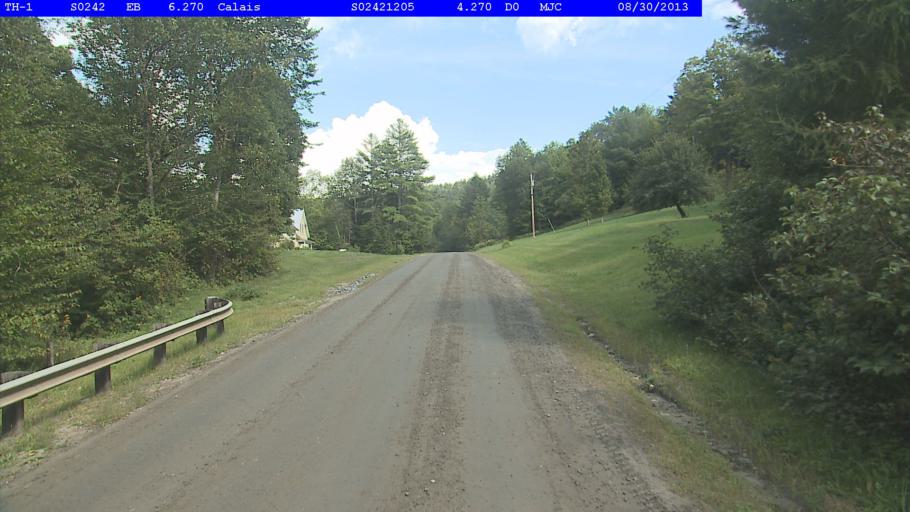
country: US
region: Vermont
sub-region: Washington County
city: Montpelier
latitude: 44.3700
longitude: -72.4657
